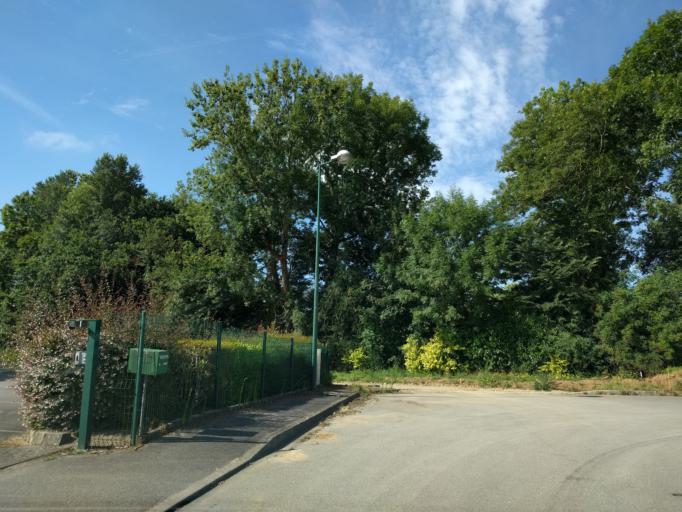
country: FR
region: Brittany
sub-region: Departement du Finistere
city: Quimper
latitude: 48.0081
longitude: -4.0700
